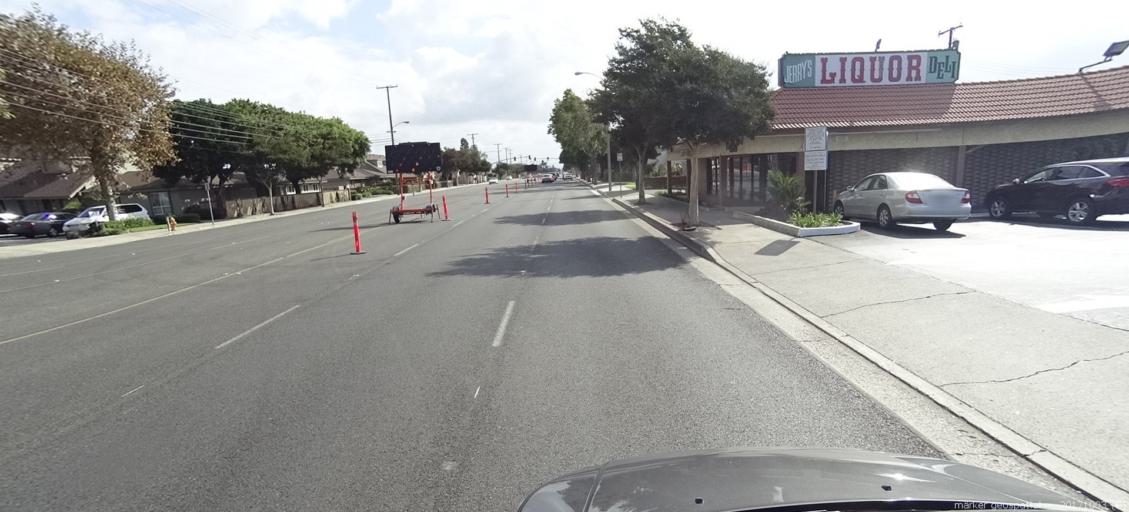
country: US
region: California
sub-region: Orange County
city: Garden Grove
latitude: 33.7595
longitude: -117.9496
